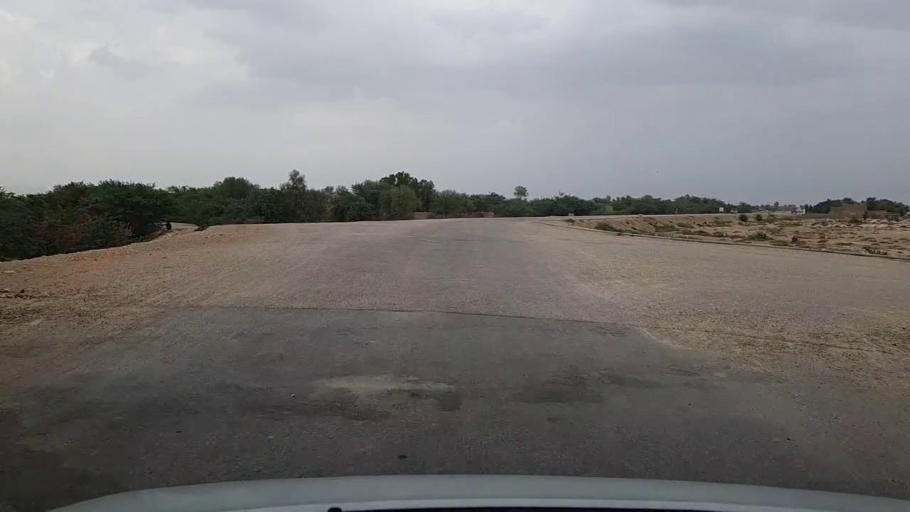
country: PK
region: Sindh
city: Sehwan
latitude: 26.3379
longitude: 67.7275
